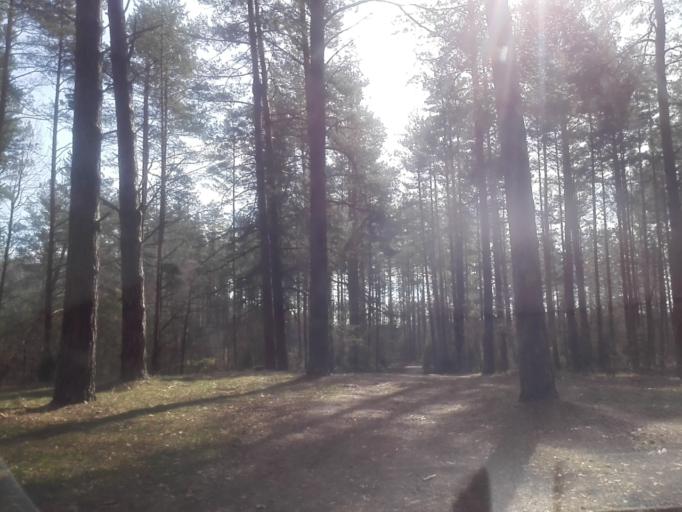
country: PL
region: Podlasie
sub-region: Powiat sejnenski
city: Sejny
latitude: 54.0279
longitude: 23.4119
